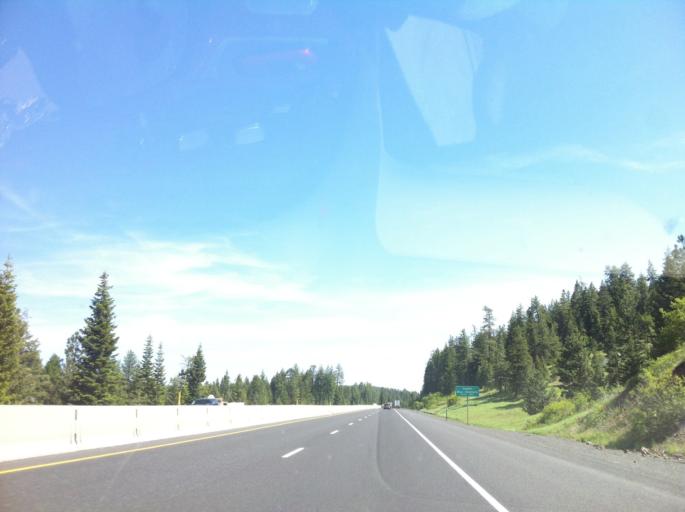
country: US
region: Oregon
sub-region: Umatilla County
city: Mission
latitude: 45.4784
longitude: -118.4003
